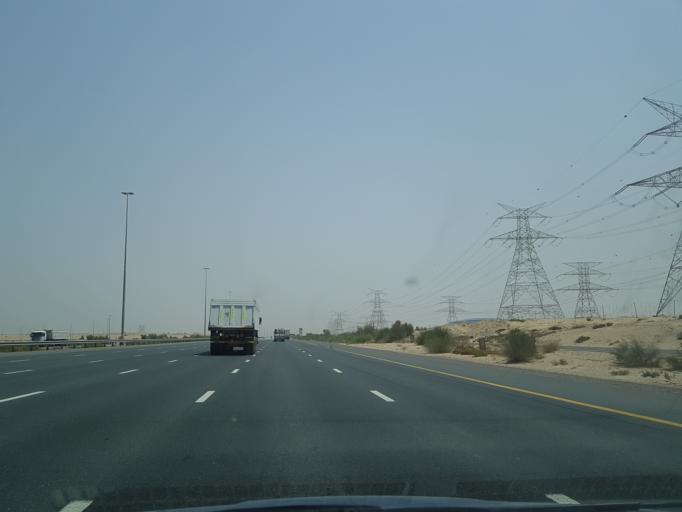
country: AE
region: Dubai
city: Dubai
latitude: 25.0458
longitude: 55.3057
